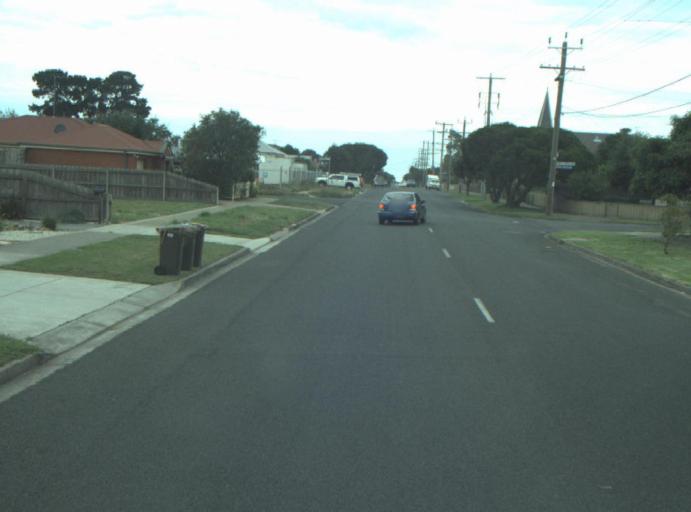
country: AU
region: Victoria
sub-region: Greater Geelong
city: Breakwater
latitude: -38.1826
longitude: 144.3892
